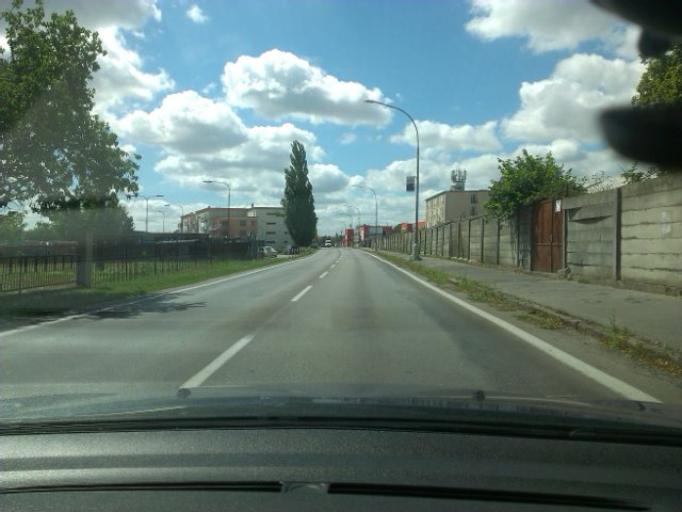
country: SK
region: Trnavsky
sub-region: Okres Trnava
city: Piestany
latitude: 48.6089
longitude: 17.8332
